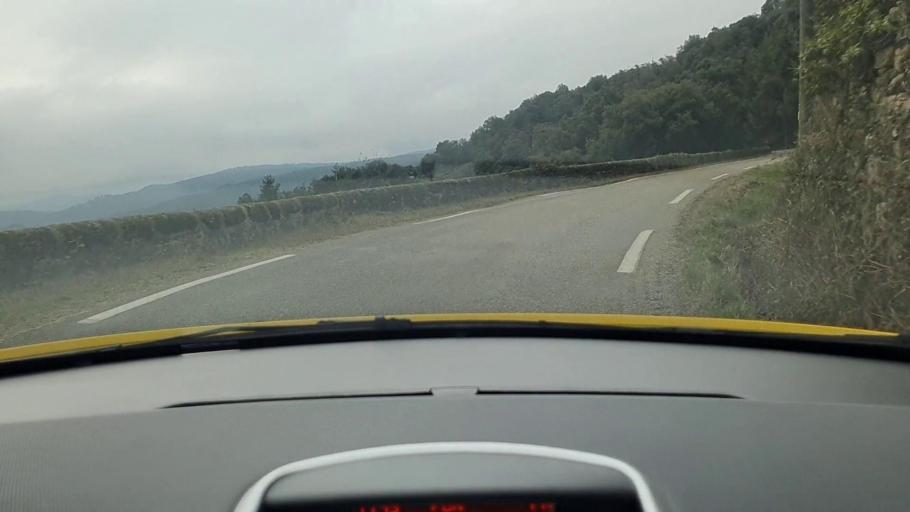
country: FR
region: Languedoc-Roussillon
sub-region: Departement du Gard
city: Besseges
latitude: 44.3464
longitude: 4.0333
